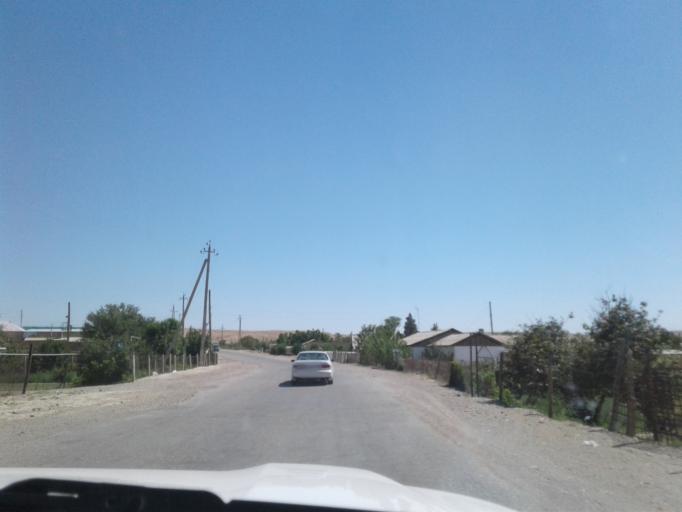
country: AF
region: Badghis
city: Bala Murghab
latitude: 35.9566
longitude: 62.9053
